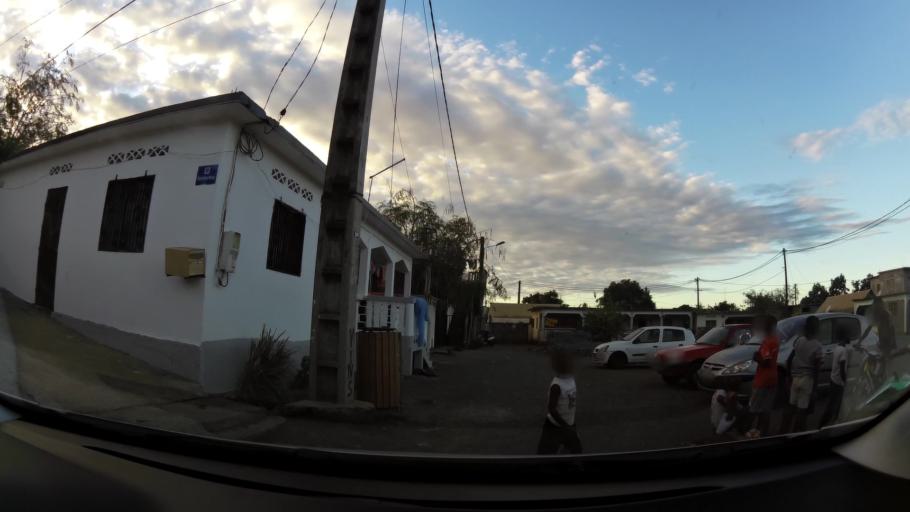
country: YT
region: Koungou
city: Koungou
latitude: -12.7307
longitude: 45.1866
